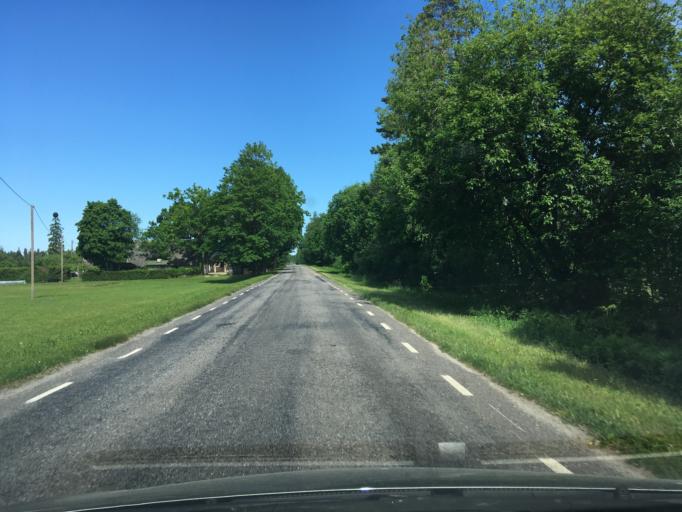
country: EE
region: Raplamaa
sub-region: Rapla vald
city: Rapla
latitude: 59.0598
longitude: 24.9107
